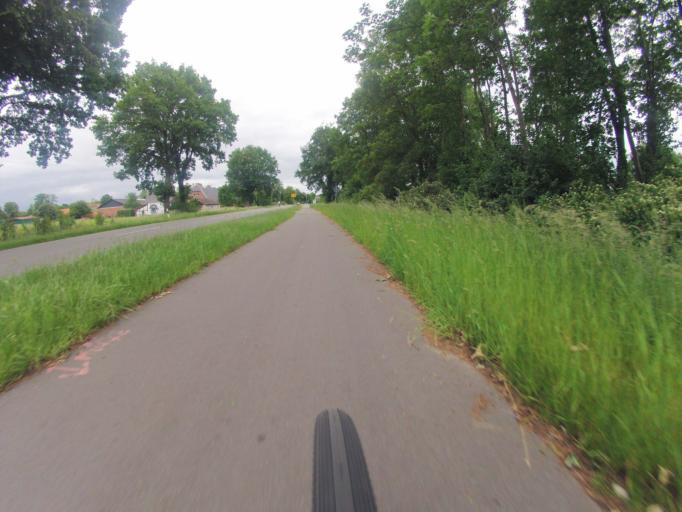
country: DE
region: North Rhine-Westphalia
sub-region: Regierungsbezirk Munster
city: Birgte
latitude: 52.2344
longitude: 7.6911
